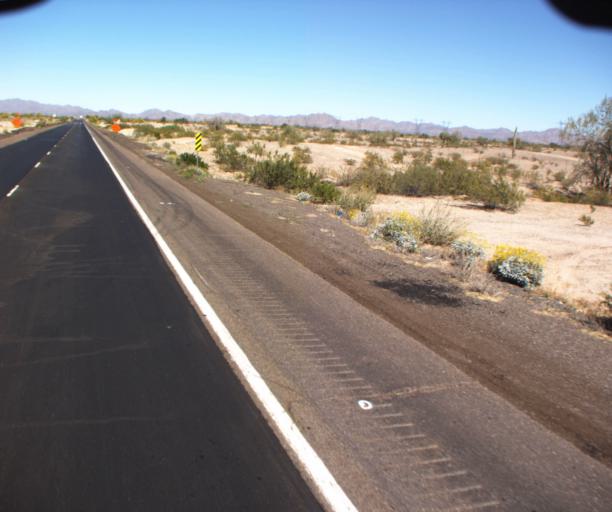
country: US
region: Arizona
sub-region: Maricopa County
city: Gila Bend
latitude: 32.9786
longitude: -112.6692
